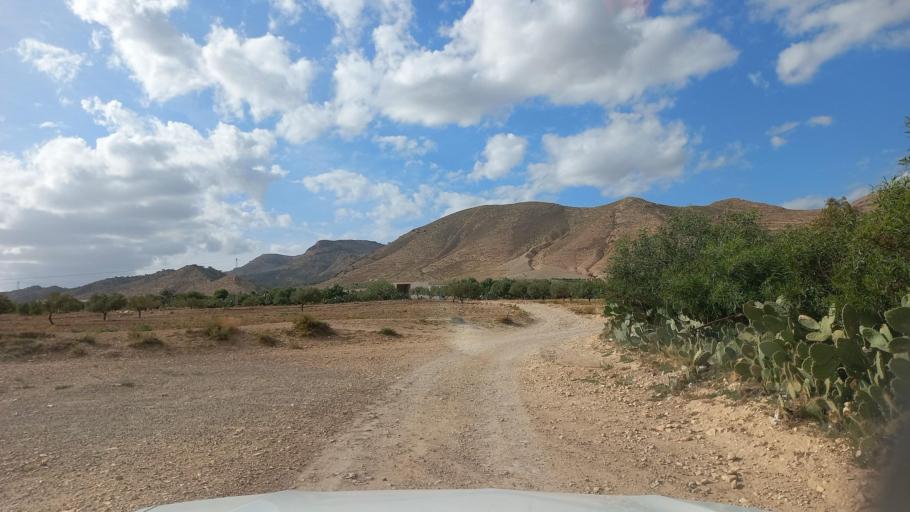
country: TN
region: Al Qasrayn
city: Sbiba
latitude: 35.4508
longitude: 9.0727
